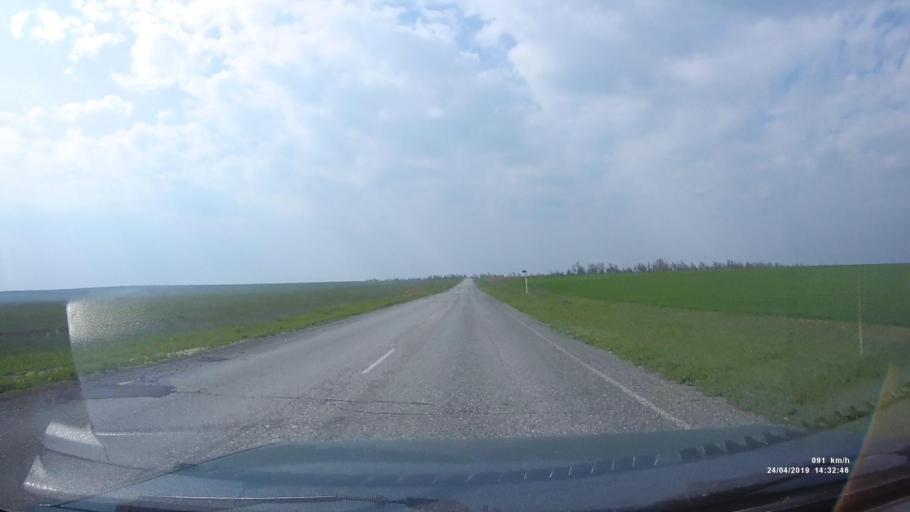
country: RU
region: Kalmykiya
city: Arshan'
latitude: 46.3674
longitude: 43.9642
